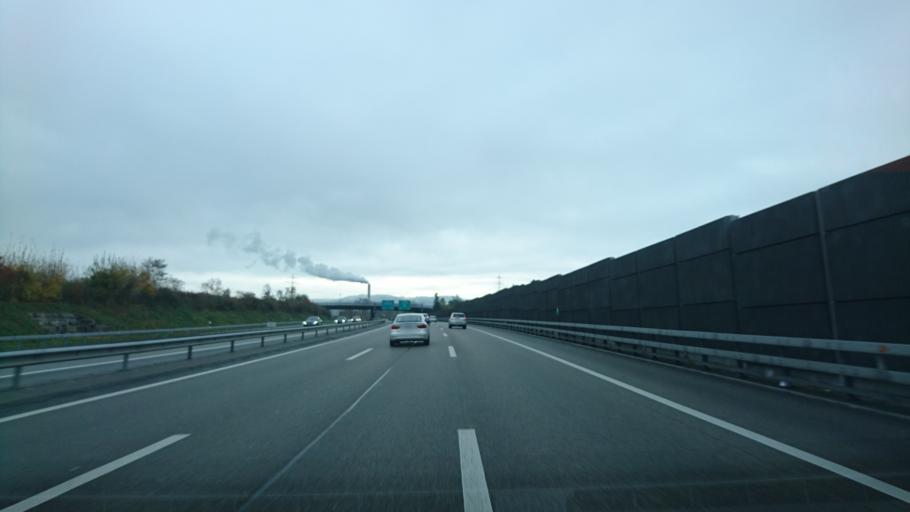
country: CH
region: Aargau
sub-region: Bezirk Zofingen
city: Oftringen
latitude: 47.3056
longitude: 7.9117
